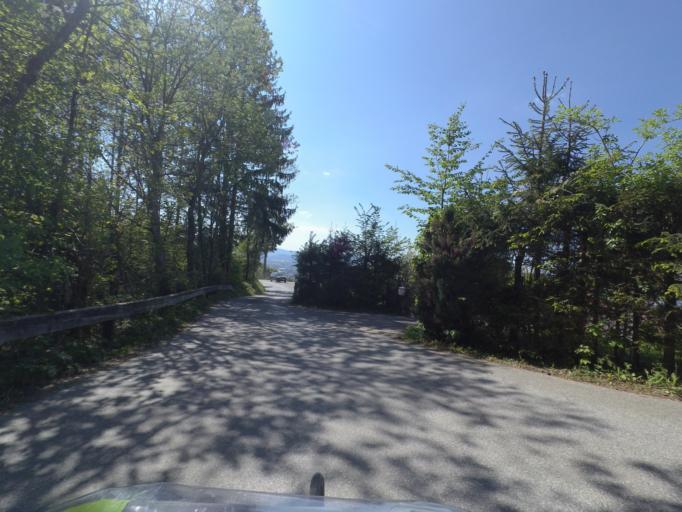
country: AT
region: Salzburg
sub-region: Politischer Bezirk Salzburg-Umgebung
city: Hallwang
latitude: 47.8215
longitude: 13.0857
